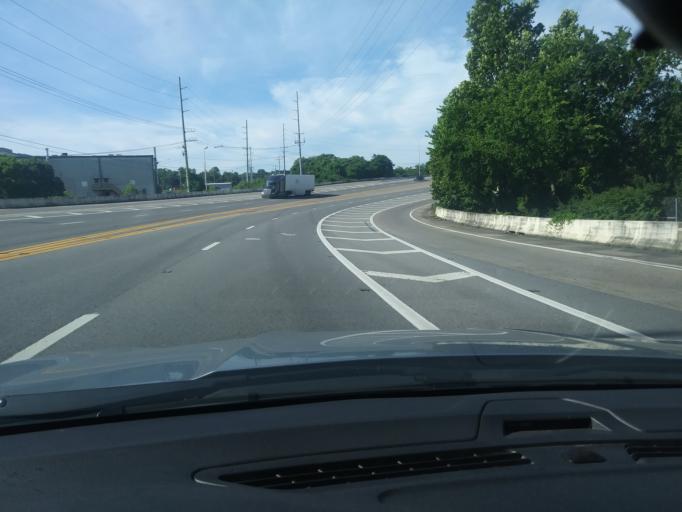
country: US
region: Tennessee
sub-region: Davidson County
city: Oak Hill
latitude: 36.1207
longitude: -86.6969
